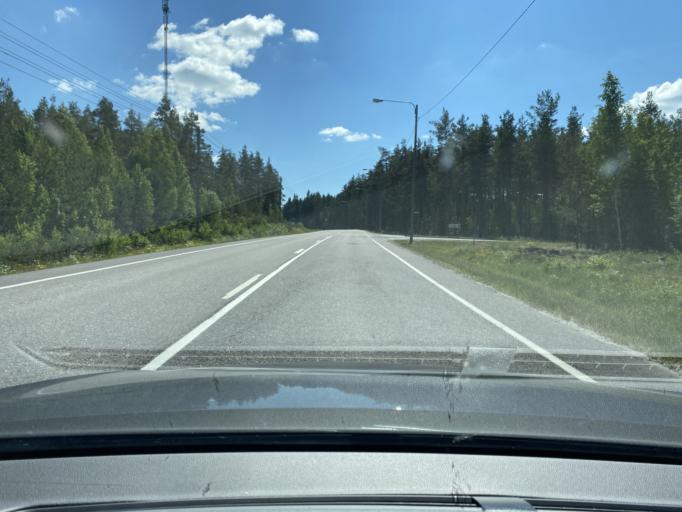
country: FI
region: Satakunta
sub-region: Rauma
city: Eura
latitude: 61.1327
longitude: 22.1727
